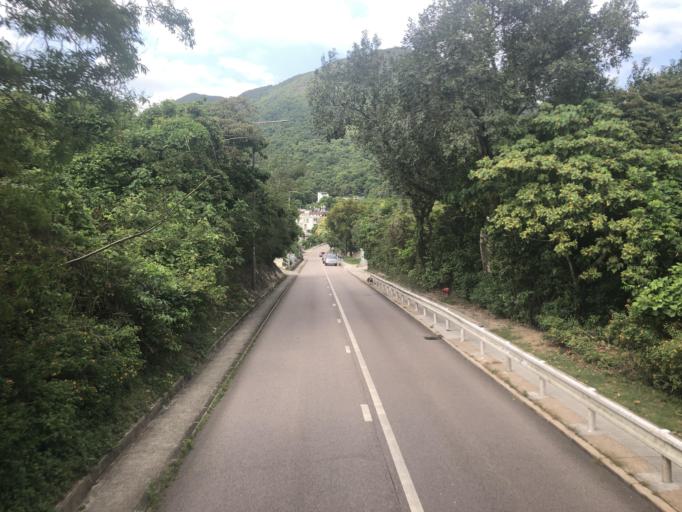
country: HK
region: Sai Kung
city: Sai Kung
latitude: 22.3898
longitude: 114.3076
